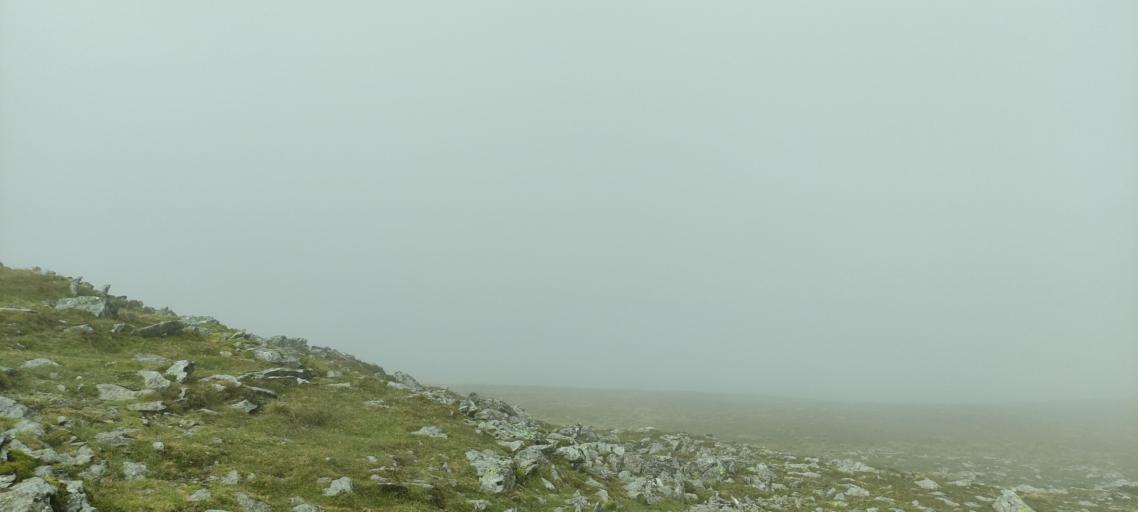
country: GB
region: England
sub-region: Cumbria
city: Ambleside
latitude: 54.5121
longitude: -2.9757
